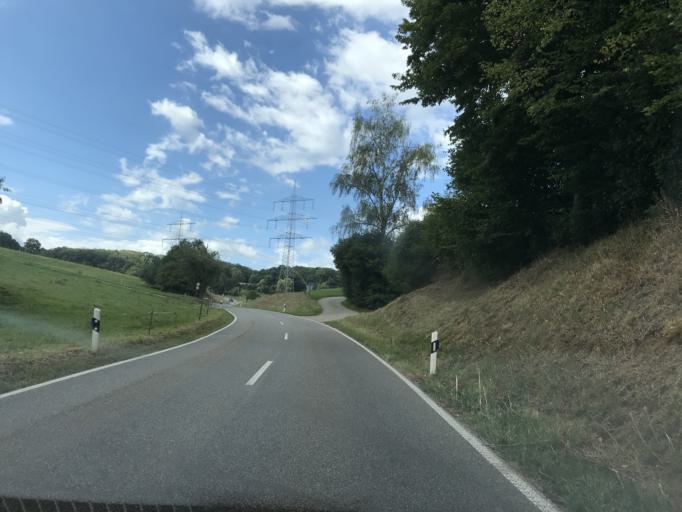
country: DE
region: Baden-Wuerttemberg
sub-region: Freiburg Region
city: Maulburg
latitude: 47.6291
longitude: 7.7751
